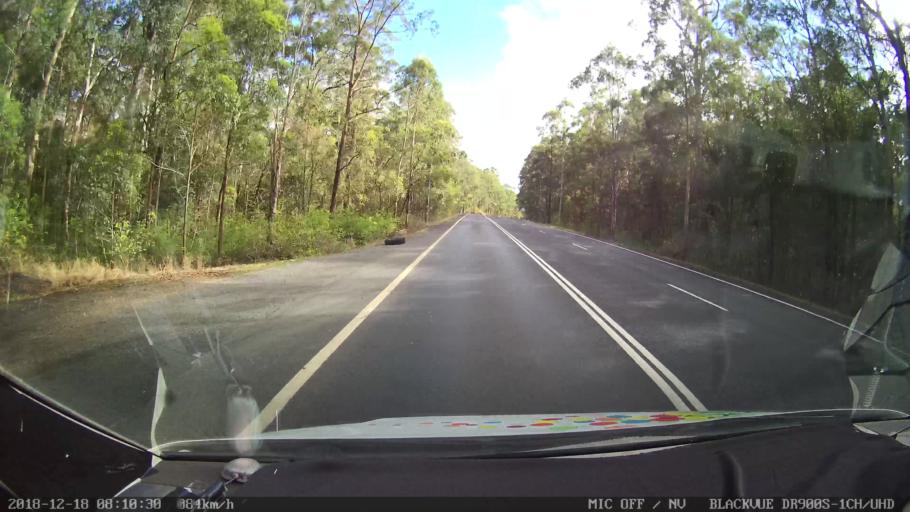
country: AU
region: New South Wales
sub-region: Kyogle
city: Kyogle
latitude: -28.3607
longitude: 152.6620
